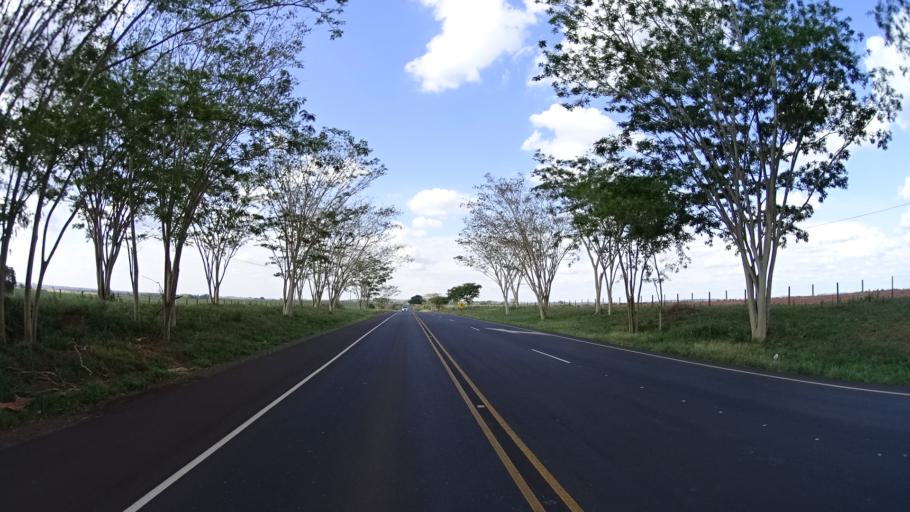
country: BR
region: Sao Paulo
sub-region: Urupes
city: Urupes
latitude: -21.0365
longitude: -49.2408
